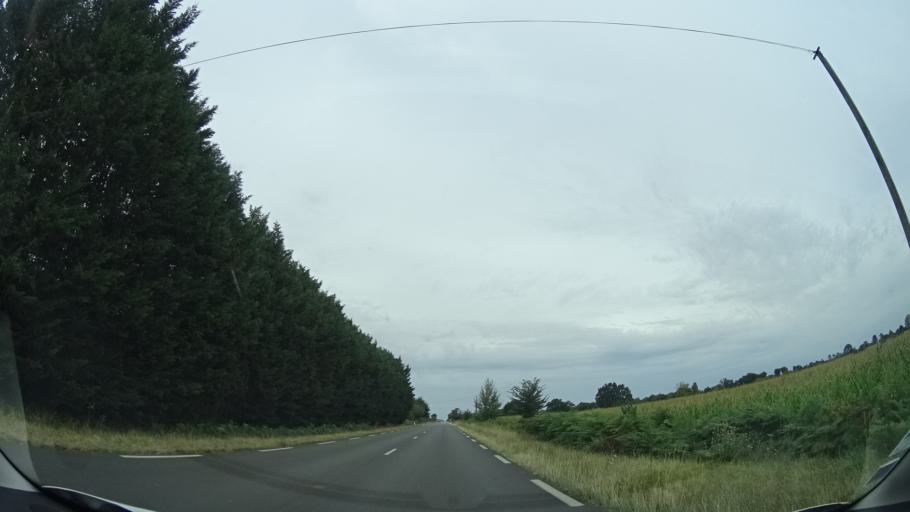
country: FR
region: Pays de la Loire
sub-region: Departement de la Mayenne
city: Meslay-du-Maine
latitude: 47.9637
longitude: -0.5783
